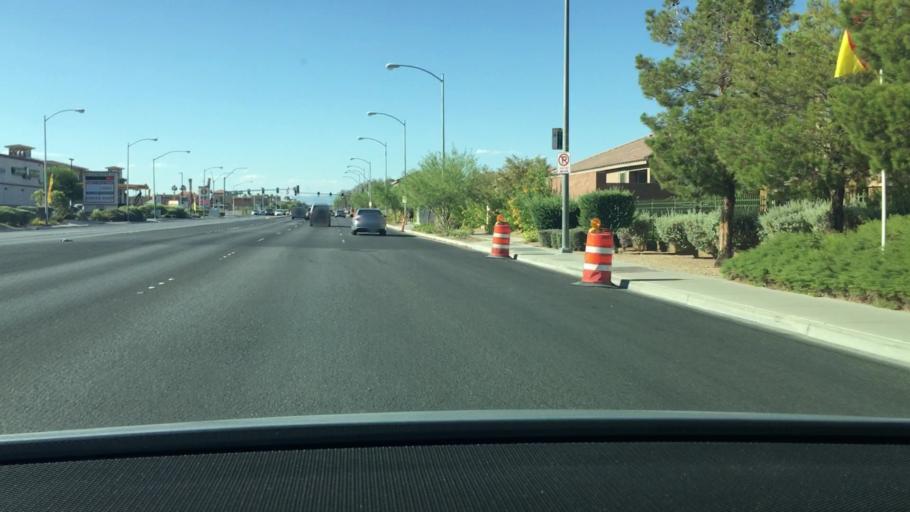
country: US
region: Nevada
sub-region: Clark County
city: Summerlin South
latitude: 36.0905
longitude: -115.2973
